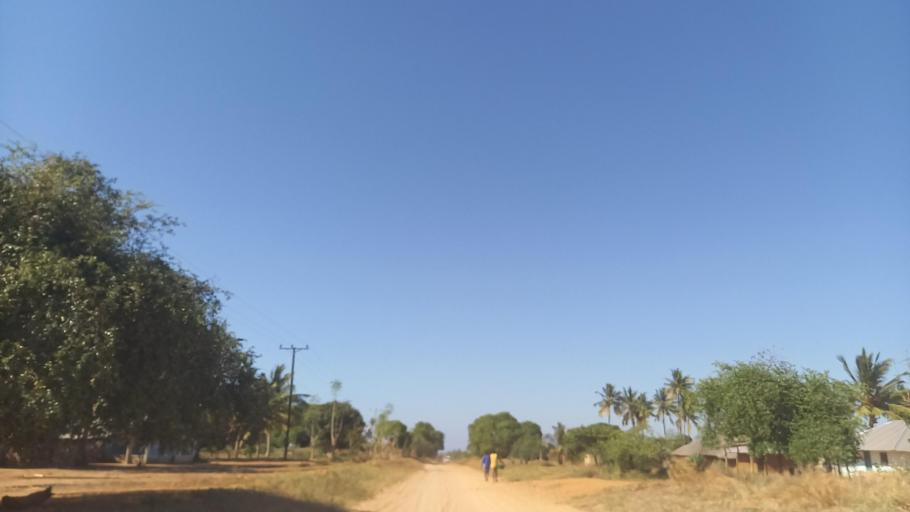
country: MZ
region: Cabo Delgado
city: Pemba
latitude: -13.1509
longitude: 40.5573
